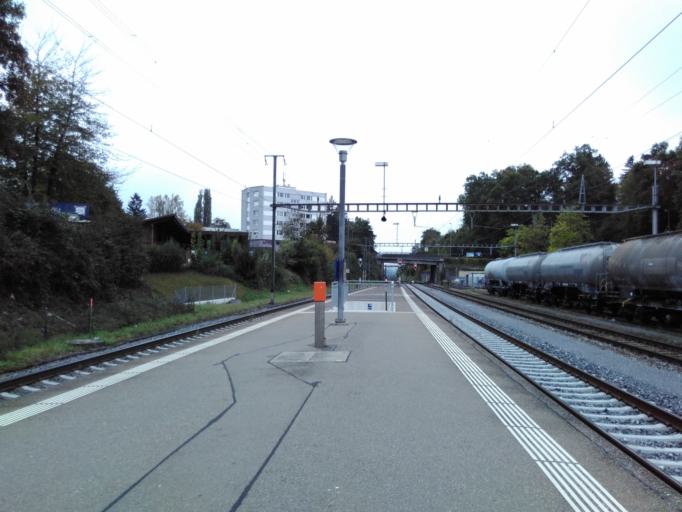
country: CH
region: Zurich
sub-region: Bezirk Buelach
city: Kloten
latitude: 47.4474
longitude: 8.5817
